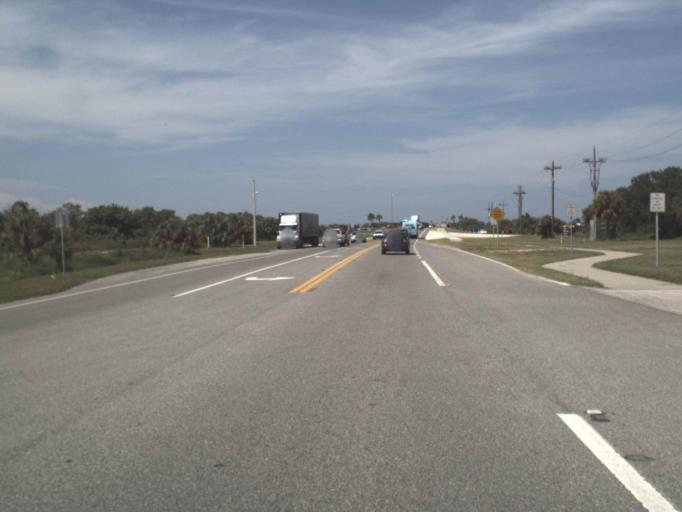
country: US
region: Florida
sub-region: Manatee County
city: Holmes Beach
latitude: 27.4963
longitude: -82.6864
